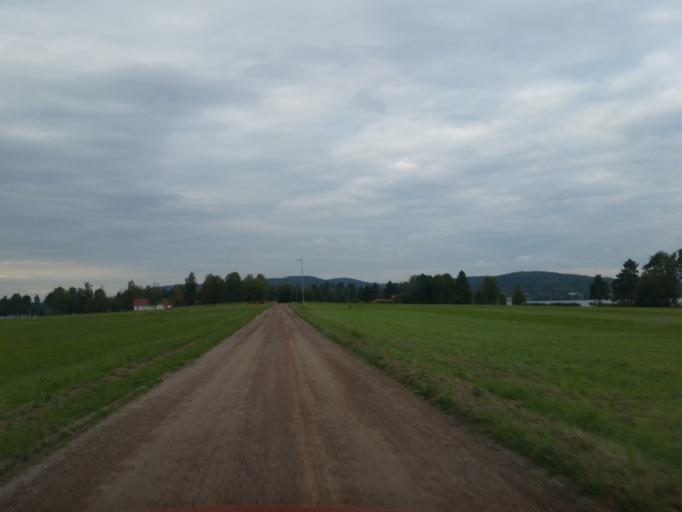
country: SE
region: Dalarna
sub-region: Leksand Municipality
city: Smedby
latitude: 60.6776
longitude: 15.1389
